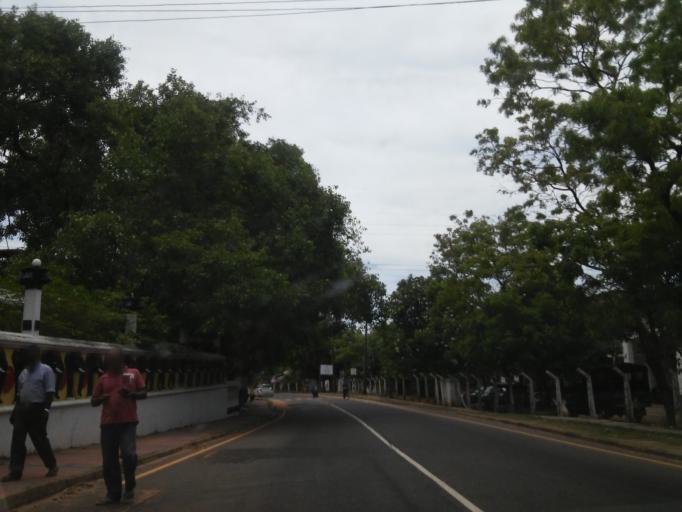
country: LK
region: Eastern Province
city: Trincomalee
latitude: 8.5915
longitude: 81.2161
